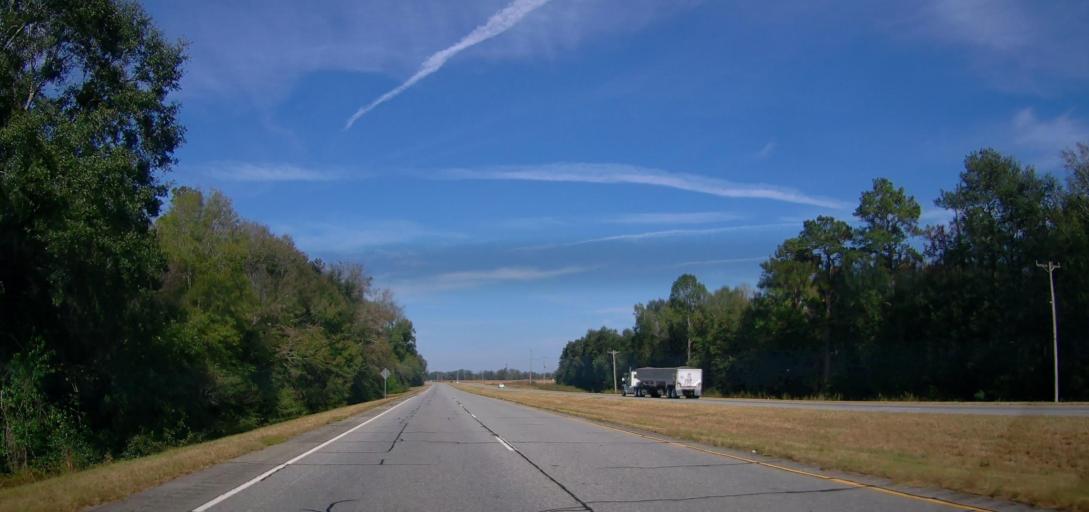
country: US
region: Georgia
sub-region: Dougherty County
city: Putney
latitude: 31.3555
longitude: -84.1593
